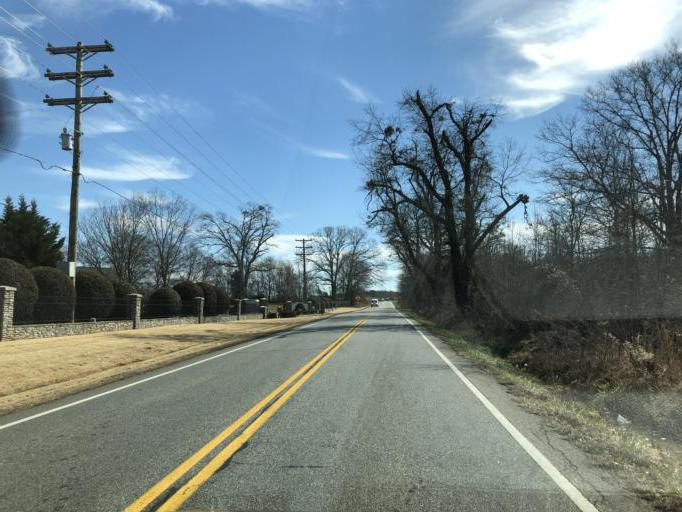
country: US
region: South Carolina
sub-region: Spartanburg County
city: Boiling Springs
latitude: 35.0521
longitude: -81.9297
